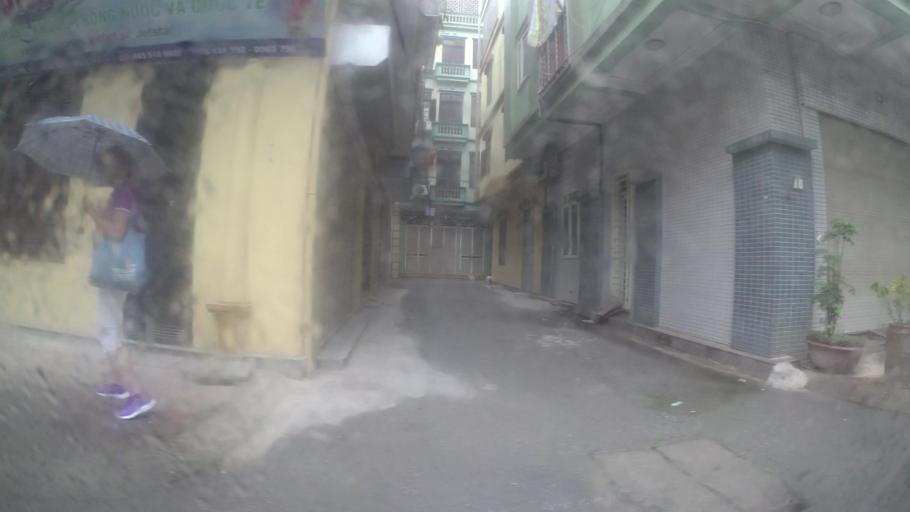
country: VN
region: Ha Noi
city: Cau Giay
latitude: 21.0188
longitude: 105.7904
